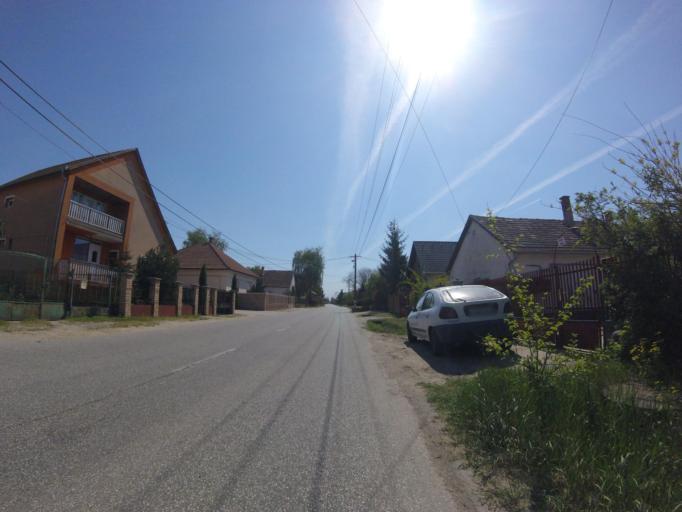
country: HU
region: Pest
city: Hernad
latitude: 47.1612
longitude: 19.4361
